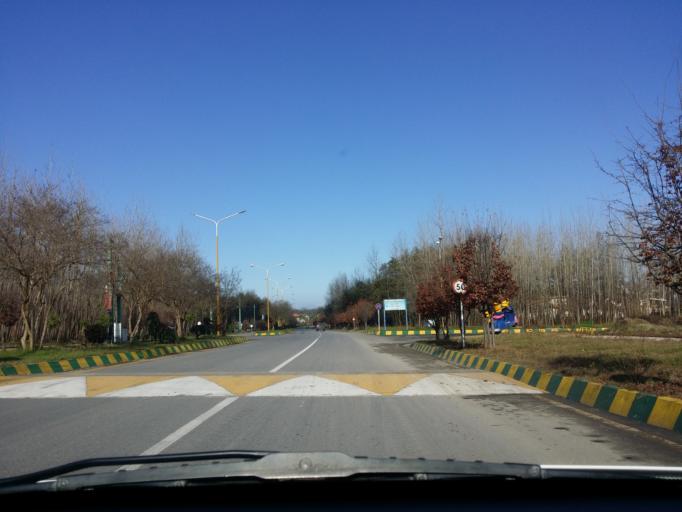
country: IR
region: Mazandaran
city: Chalus
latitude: 36.6779
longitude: 51.3066
